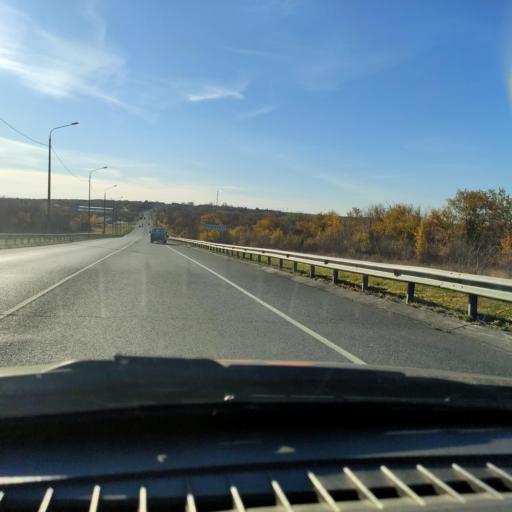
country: RU
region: Samara
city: Mezhdurechensk
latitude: 53.2534
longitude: 49.0377
